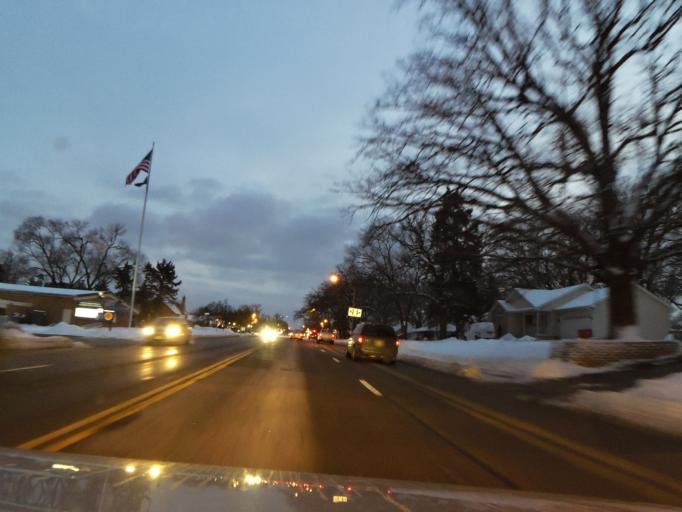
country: US
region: Minnesota
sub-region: Hennepin County
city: Richfield
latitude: 44.8859
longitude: -93.2679
